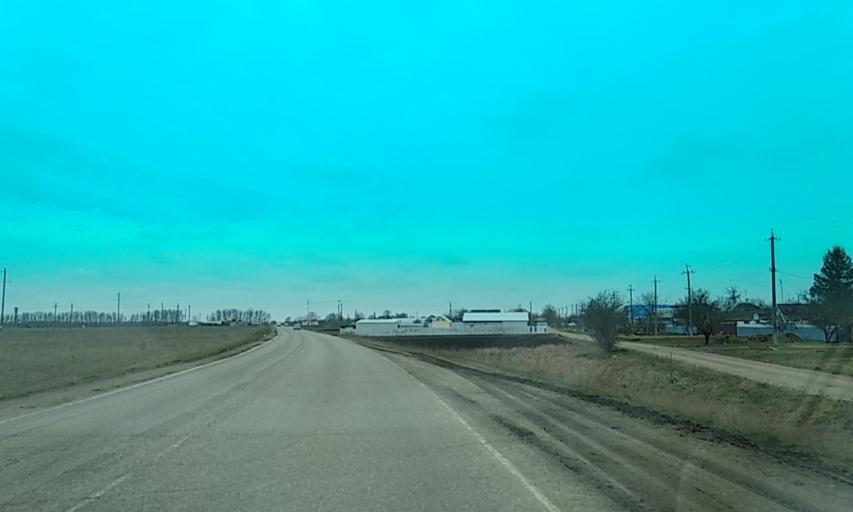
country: RU
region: Krasnodarskiy
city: Ust'-Labinsk
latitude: 45.3702
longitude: 39.7080
